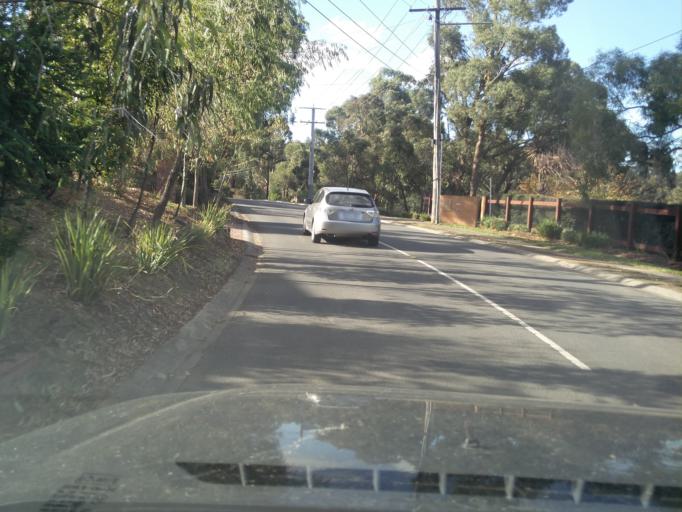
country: AU
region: Victoria
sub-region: Nillumbik
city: Eltham
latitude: -37.7218
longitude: 145.1613
